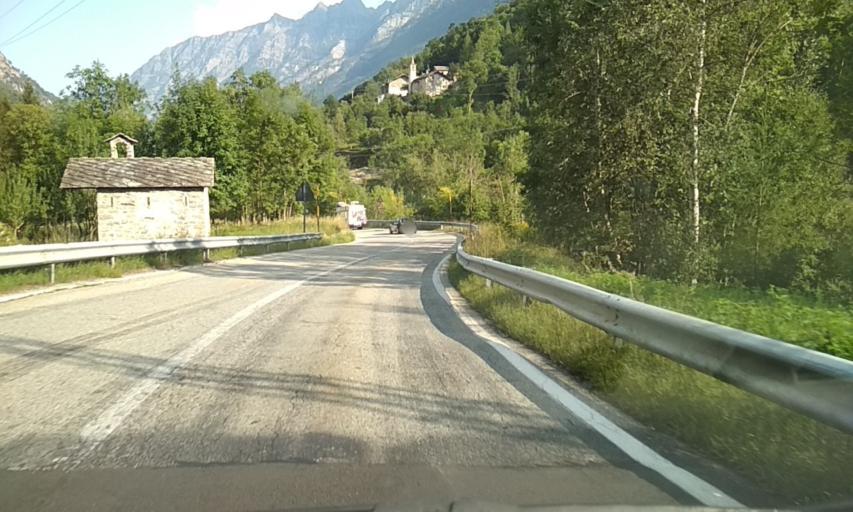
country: IT
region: Piedmont
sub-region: Provincia di Torino
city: Noasca
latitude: 45.4483
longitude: 7.3239
